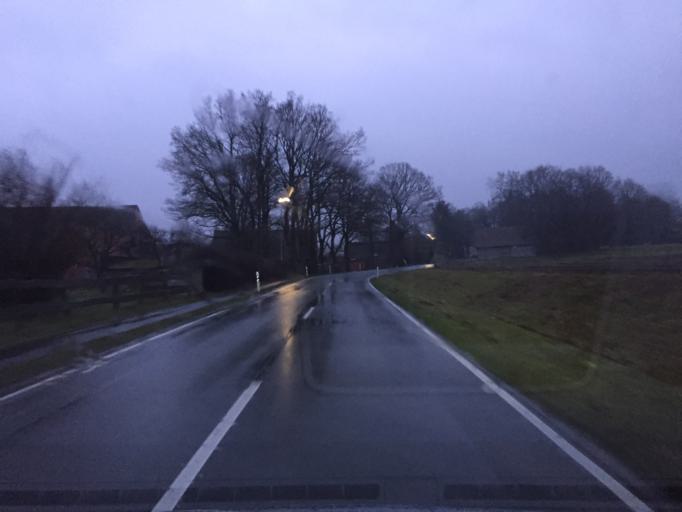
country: DE
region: Lower Saxony
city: Sudwalde
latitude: 52.8458
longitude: 8.8452
